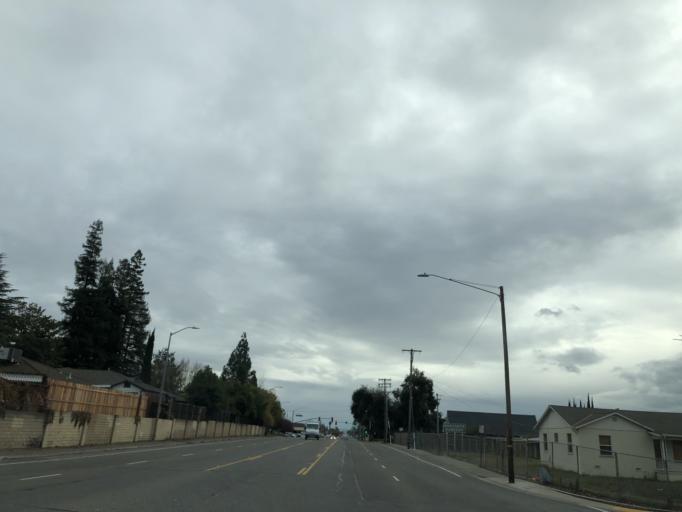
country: US
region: California
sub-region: Sacramento County
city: Carmichael
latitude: 38.6428
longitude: -121.3280
